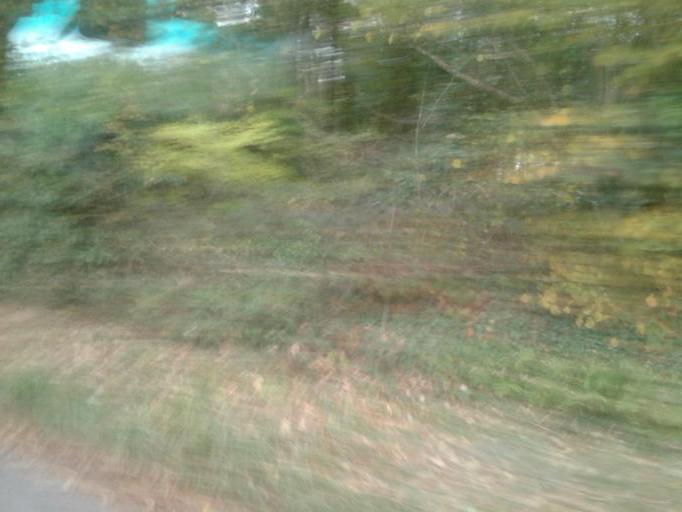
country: IE
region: Munster
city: Nenagh Bridge
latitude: 52.9550
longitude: -8.0339
